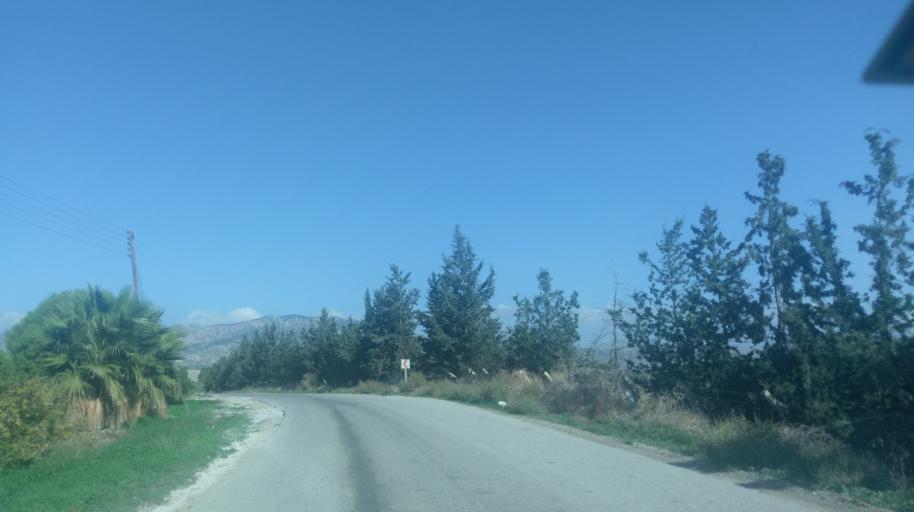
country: CY
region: Lefkosia
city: Nicosia
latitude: 35.2297
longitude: 33.4192
